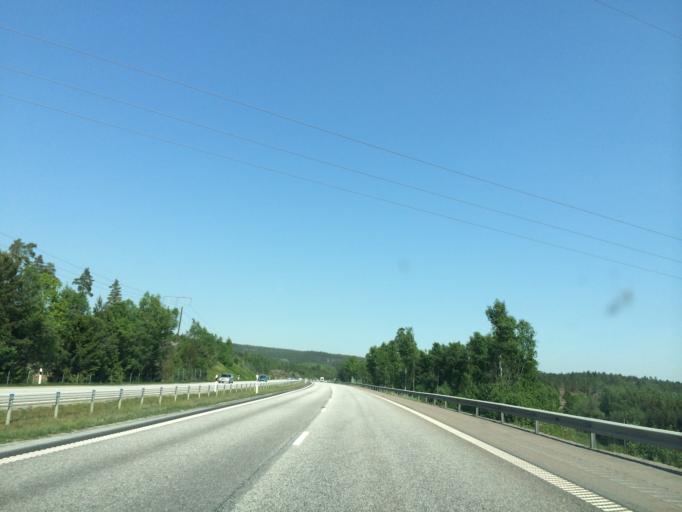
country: SE
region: OEstergoetland
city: Lindo
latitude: 58.6723
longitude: 16.2508
